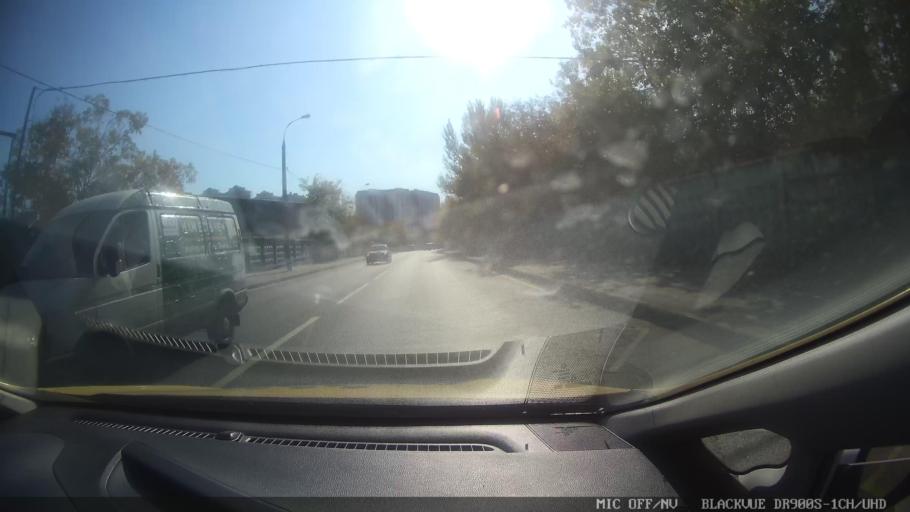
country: RU
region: Moscow
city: Tekstil'shchiki
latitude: 55.6938
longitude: 37.7137
